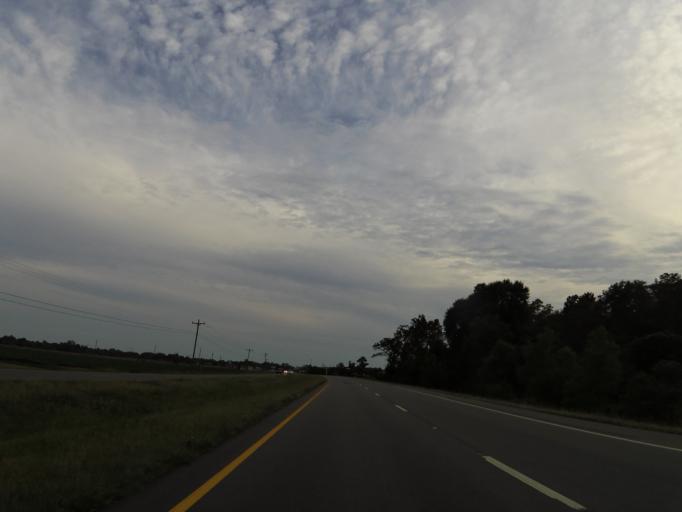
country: US
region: Alabama
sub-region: Escambia County
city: Atmore
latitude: 31.0586
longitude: -87.4926
